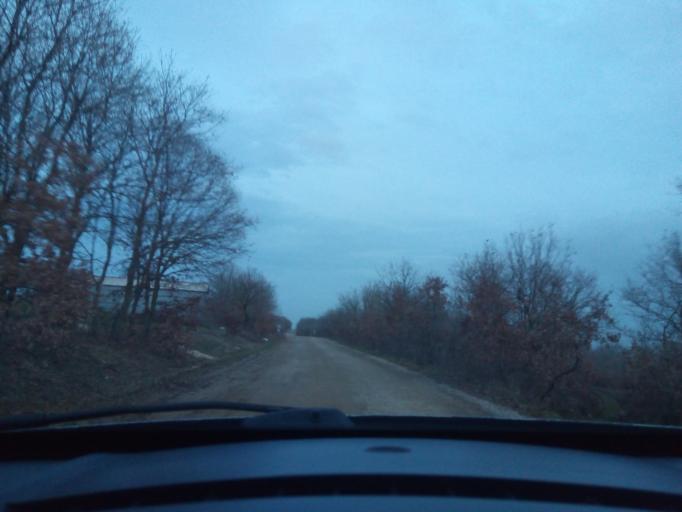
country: TR
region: Balikesir
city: Omerkoy
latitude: 39.9099
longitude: 28.0405
